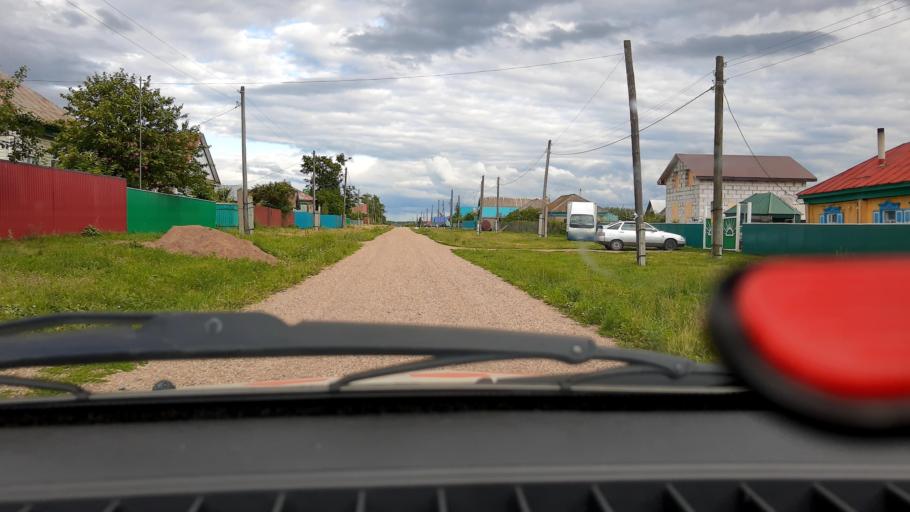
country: RU
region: Bashkortostan
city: Karmaskaly
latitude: 54.4208
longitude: 56.0240
